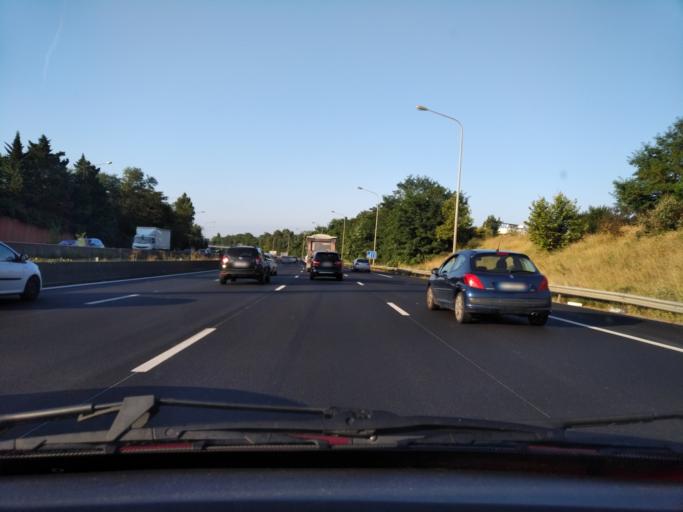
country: FR
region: Midi-Pyrenees
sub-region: Departement de la Haute-Garonne
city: Blagnac
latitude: 43.6005
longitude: 1.3977
